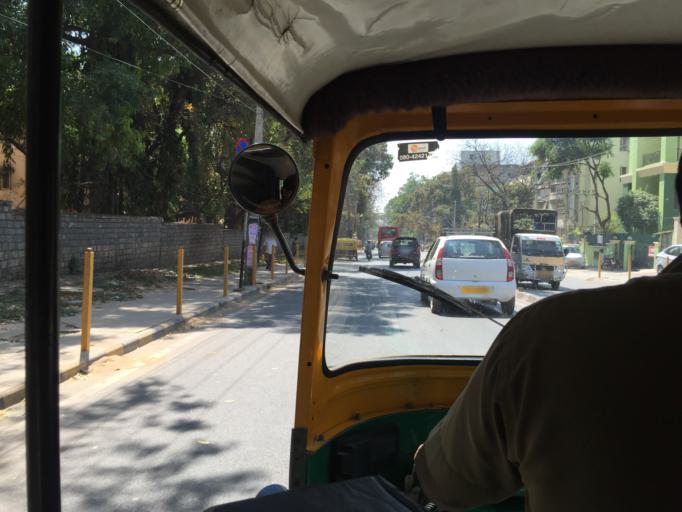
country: IN
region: Karnataka
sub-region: Bangalore Urban
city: Bangalore
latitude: 12.9770
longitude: 77.6467
